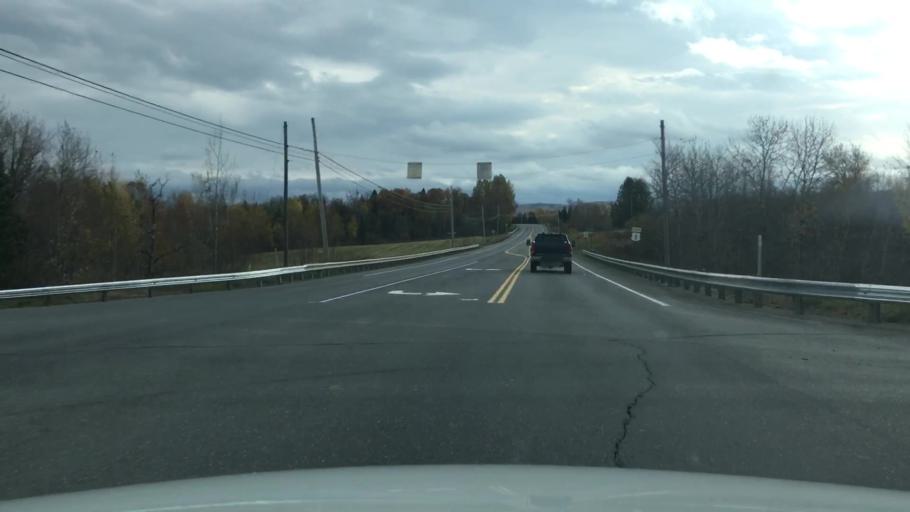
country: US
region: Maine
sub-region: Aroostook County
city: Easton
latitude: 46.5685
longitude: -67.9501
